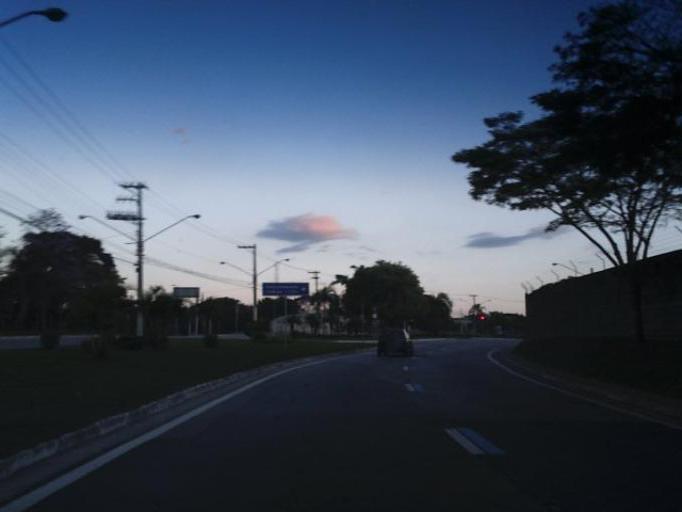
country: BR
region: Sao Paulo
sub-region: Sao Jose Dos Campos
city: Sao Jose dos Campos
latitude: -23.2178
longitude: -45.8544
